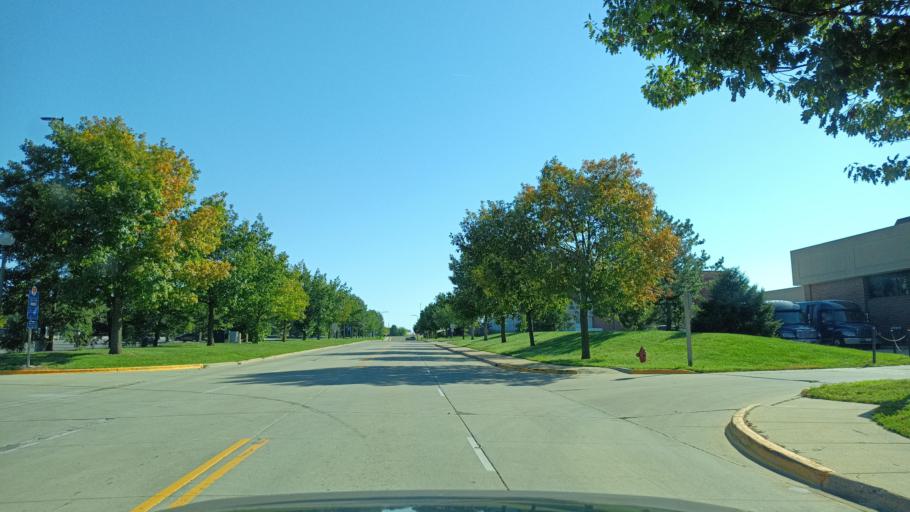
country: US
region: Illinois
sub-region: Champaign County
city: Champaign
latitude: 40.0971
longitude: -88.2416
